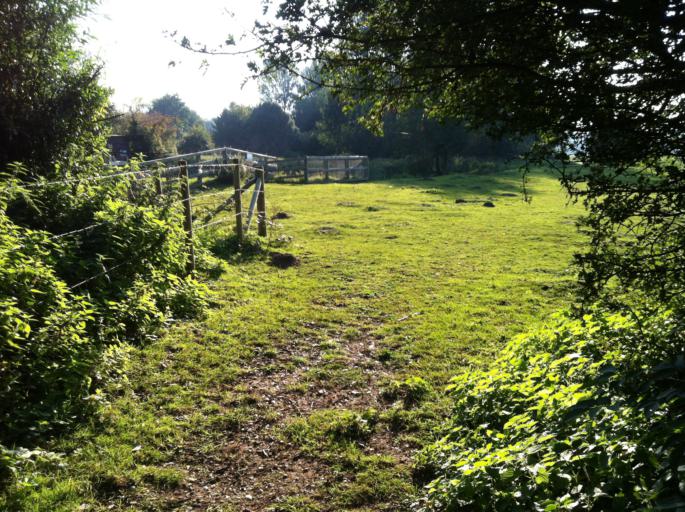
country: GB
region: England
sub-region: Norfolk
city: Bowthorpe
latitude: 52.6282
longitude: 1.2233
